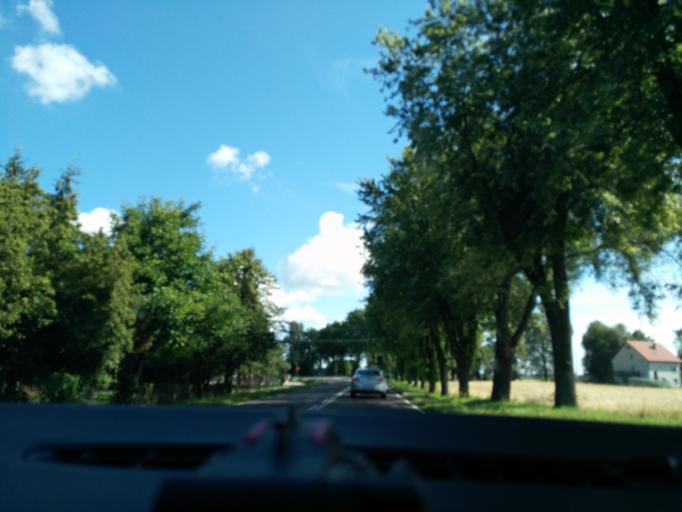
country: PL
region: Lublin Voivodeship
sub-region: Powiat radzynski
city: Radzyn Podlaski
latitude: 51.8470
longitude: 22.6979
